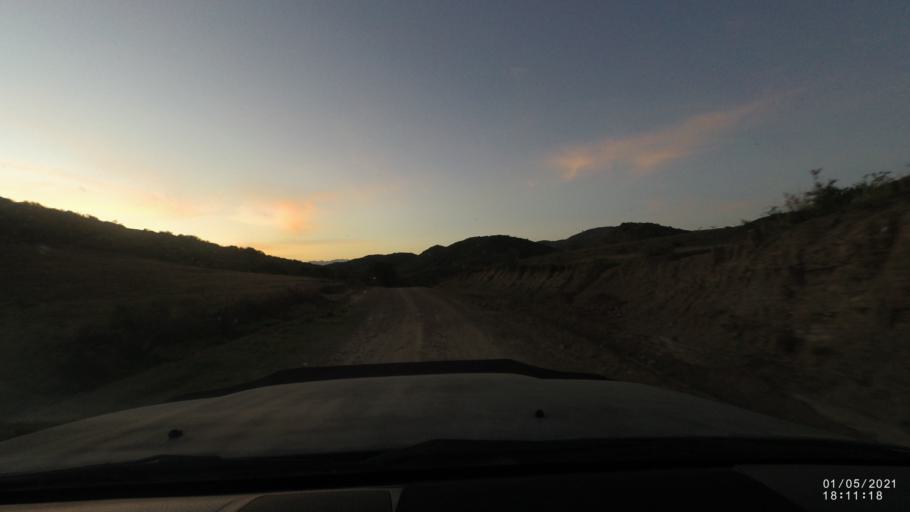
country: BO
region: Cochabamba
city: Capinota
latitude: -17.6838
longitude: -66.1993
